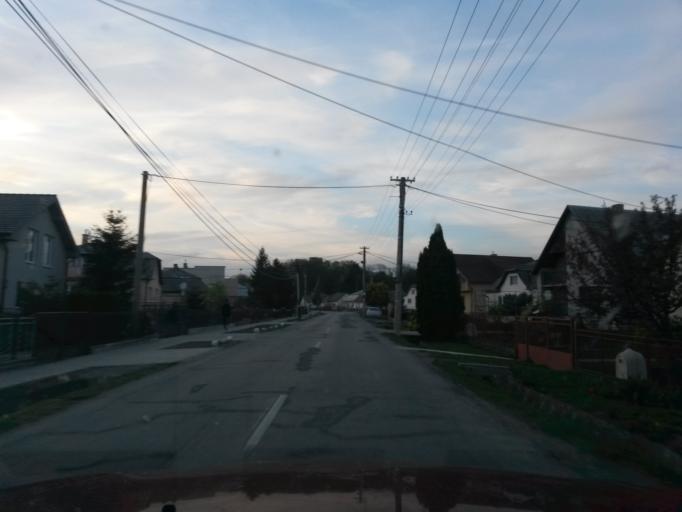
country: HU
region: Borsod-Abauj-Zemplen
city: Satoraljaujhely
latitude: 48.5219
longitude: 21.5879
